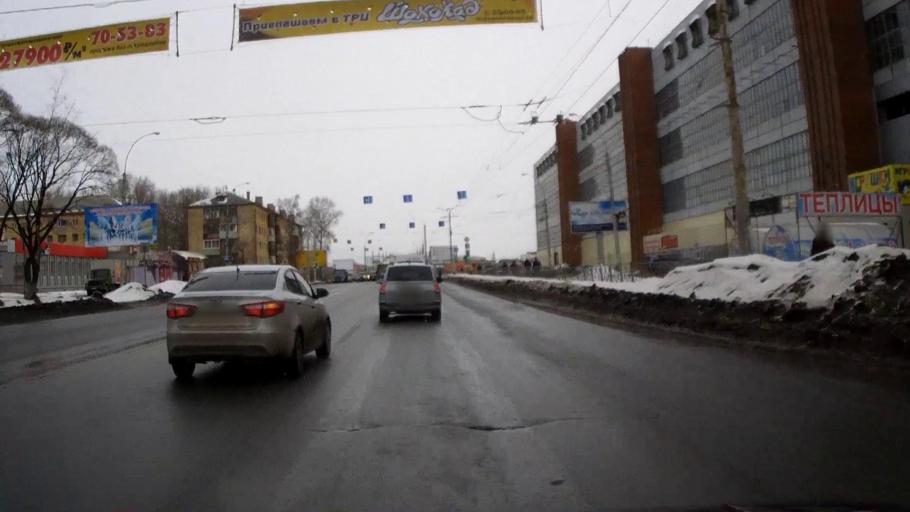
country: RU
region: Vologda
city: Vologda
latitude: 59.2128
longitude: 39.8543
